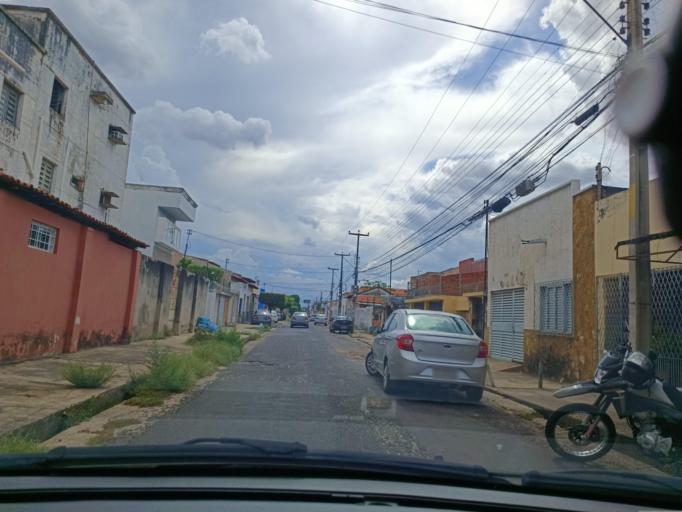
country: BR
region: Piaui
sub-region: Teresina
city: Teresina
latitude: -5.0833
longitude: -42.8104
